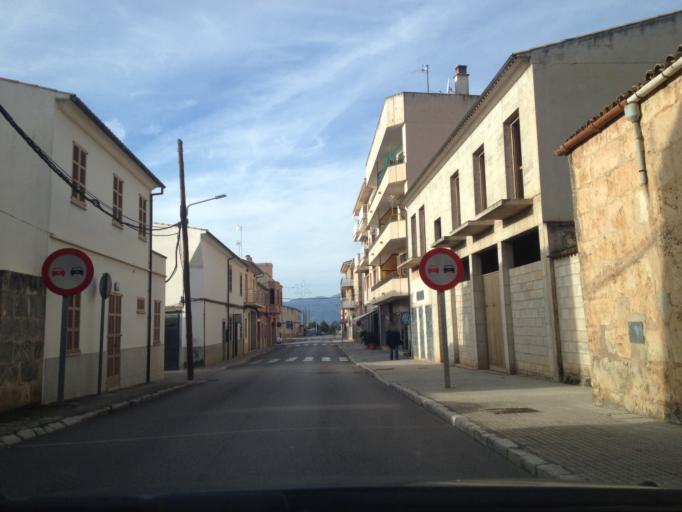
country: ES
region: Balearic Islands
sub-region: Illes Balears
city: Muro
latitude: 39.7379
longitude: 3.0544
